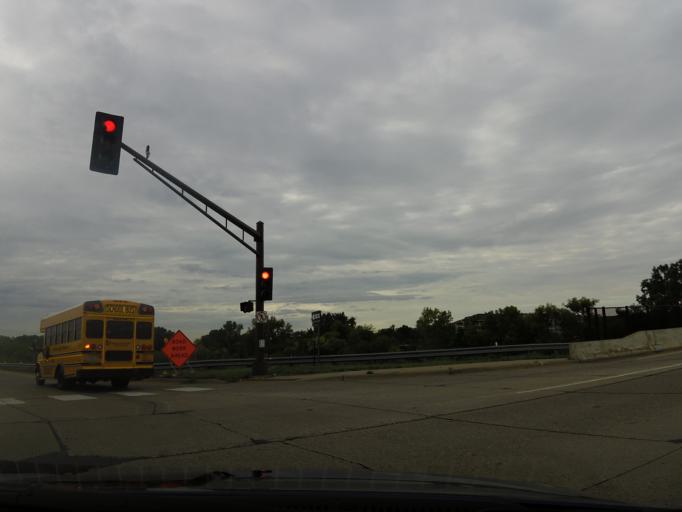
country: US
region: Minnesota
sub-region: Washington County
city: Cottage Grove
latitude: 44.8325
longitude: -92.9653
